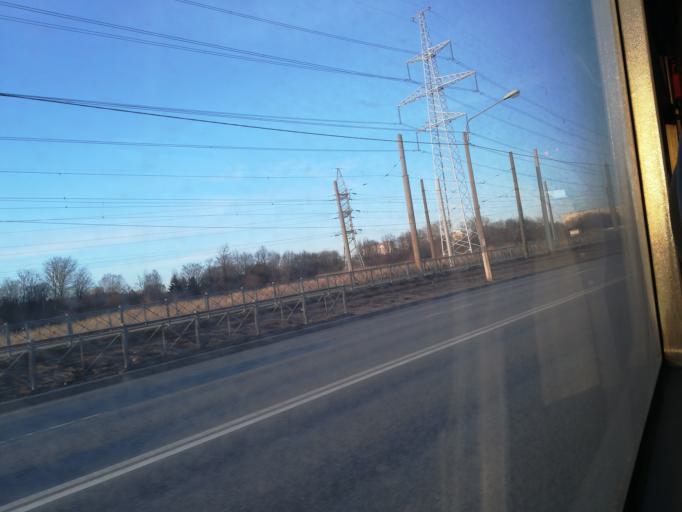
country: RU
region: St.-Petersburg
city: Uritsk
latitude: 59.8465
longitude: 30.1602
